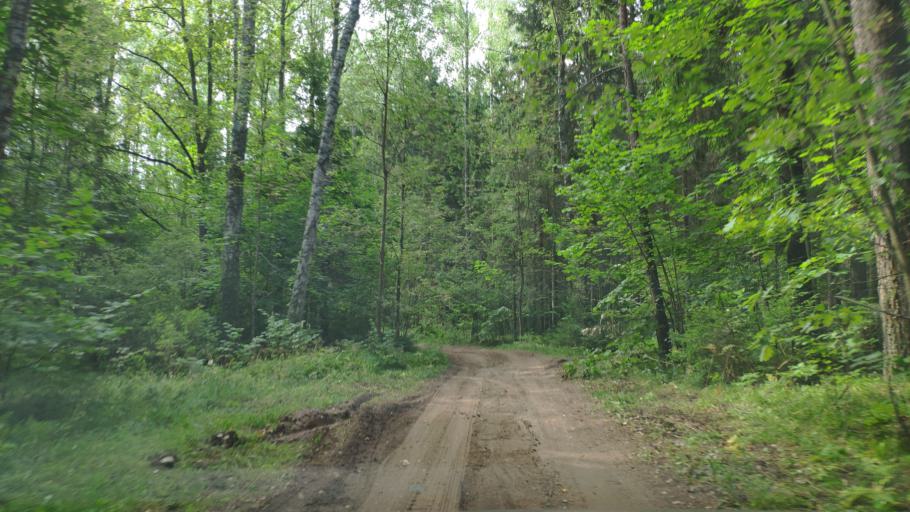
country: BY
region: Minsk
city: Zaslawye
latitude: 53.9650
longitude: 27.2971
